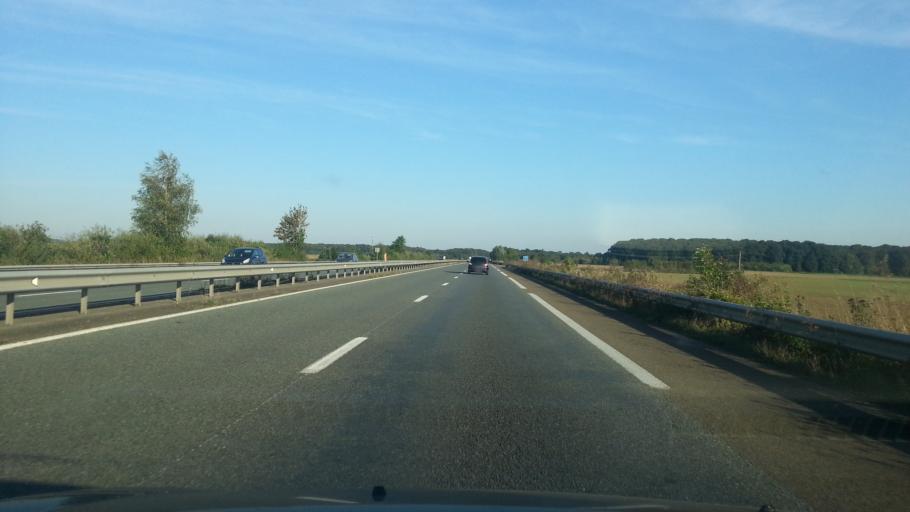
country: FR
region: Picardie
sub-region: Departement de l'Oise
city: Agnetz
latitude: 49.4116
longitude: 2.3248
